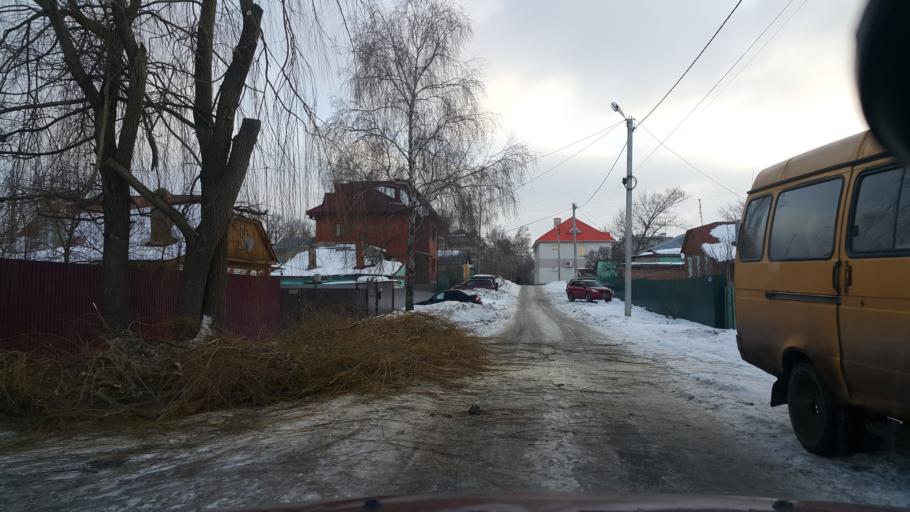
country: RU
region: Tambov
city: Kotovsk
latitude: 52.6003
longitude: 41.4943
